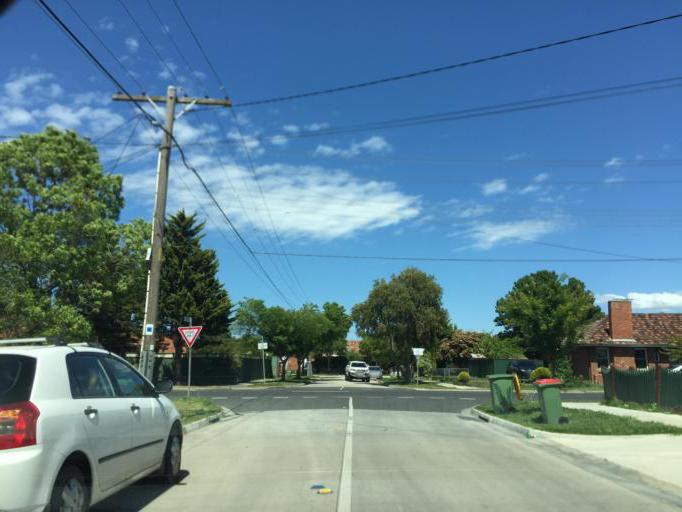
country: AU
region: Victoria
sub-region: Maribyrnong
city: Braybrook
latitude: -37.7862
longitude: 144.8471
